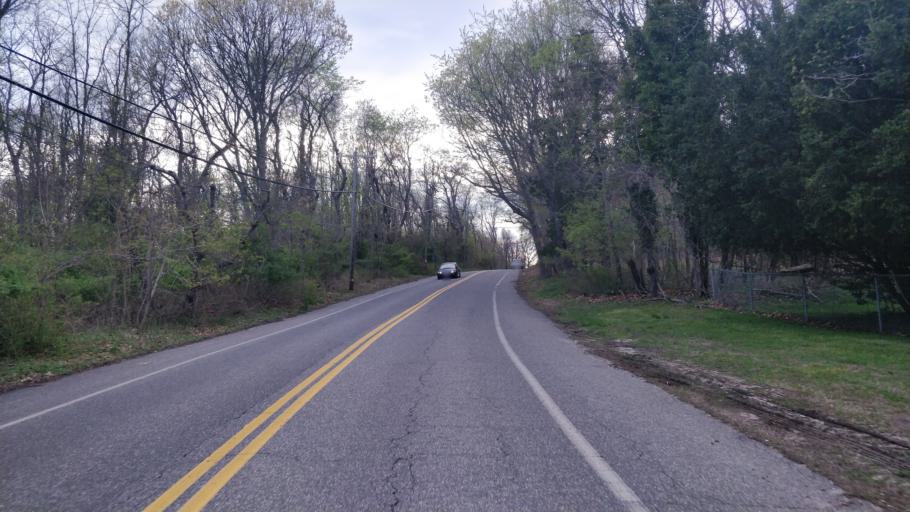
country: US
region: New York
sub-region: Suffolk County
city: Kings Park
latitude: 40.9020
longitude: -73.2440
